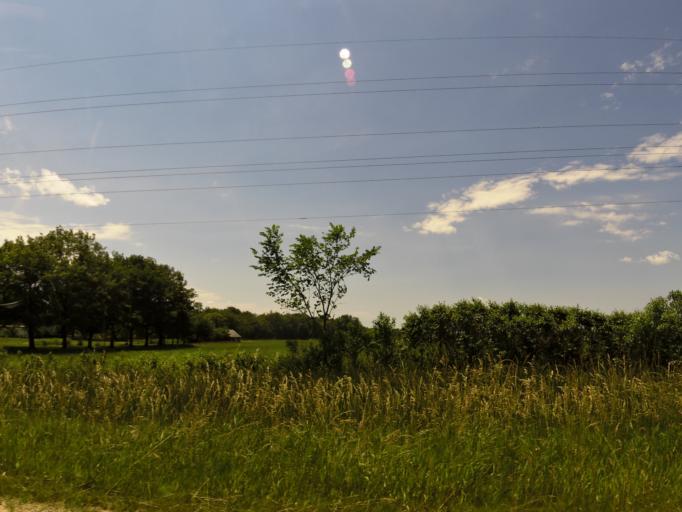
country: US
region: Iowa
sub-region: Bremer County
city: Tripoli
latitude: 42.7148
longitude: -92.1787
